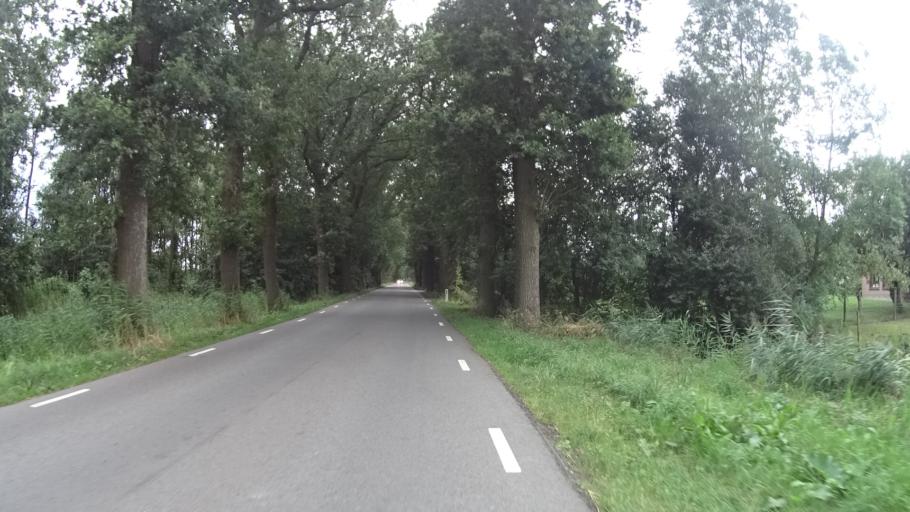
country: NL
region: Groningen
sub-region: Gemeente Slochteren
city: Slochteren
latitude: 53.2020
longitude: 6.8378
